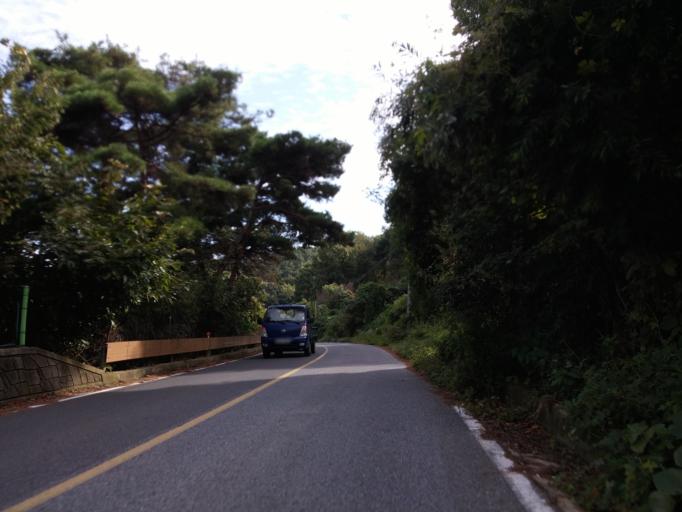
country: KR
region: Chungcheongnam-do
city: Yonmu
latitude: 36.1734
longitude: 127.1690
